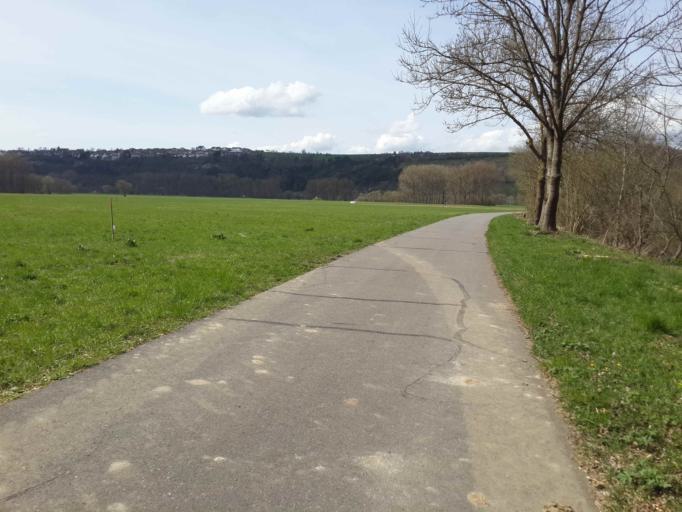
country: DE
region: Baden-Wuerttemberg
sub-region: Regierungsbezirk Stuttgart
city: Krautheim
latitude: 49.3886
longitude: 9.6588
